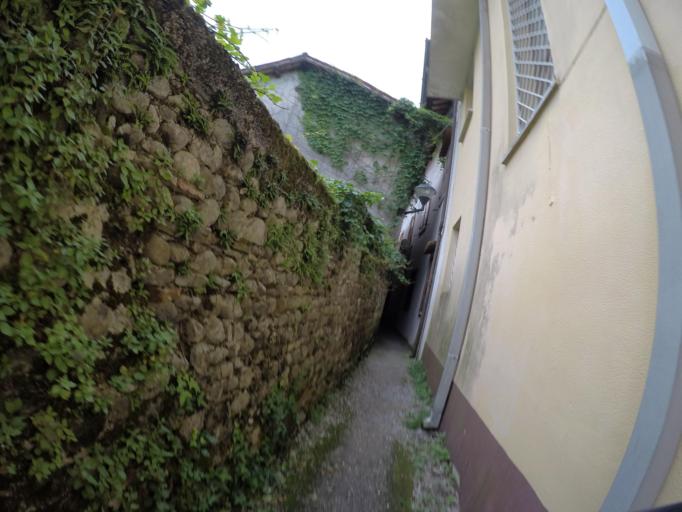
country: IT
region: Friuli Venezia Giulia
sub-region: Provincia di Udine
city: Percoto
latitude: 45.9736
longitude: 13.3189
